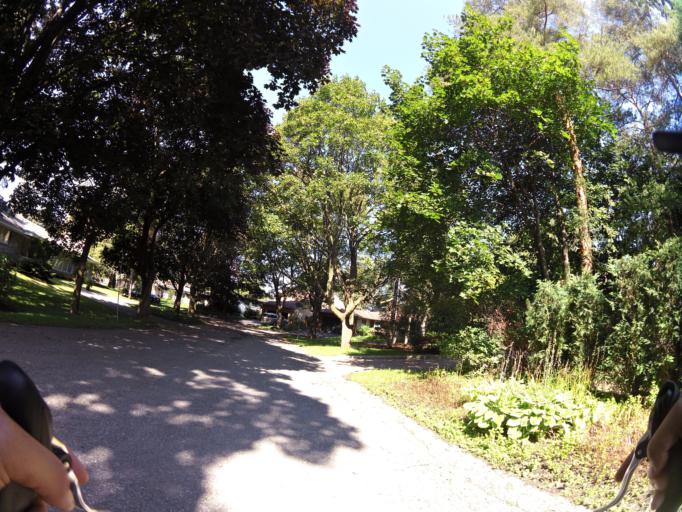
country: CA
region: Ontario
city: Ottawa
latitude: 45.3976
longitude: -75.6567
